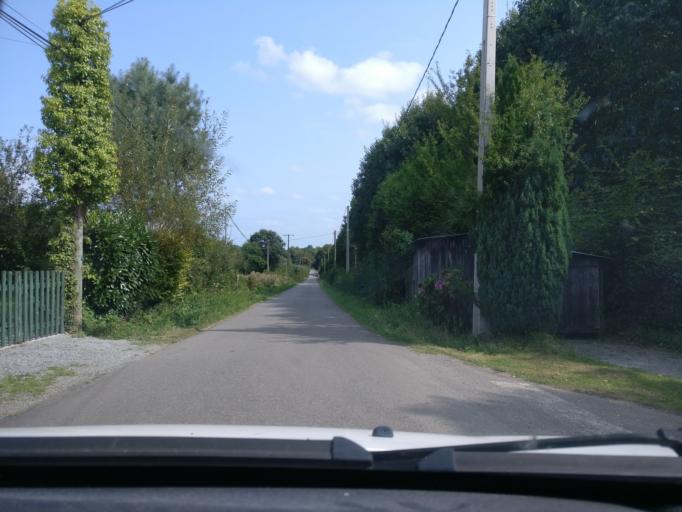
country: FR
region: Brittany
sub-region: Departement d'Ille-et-Vilaine
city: Erce-pres-Liffre
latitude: 48.2615
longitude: -1.5200
